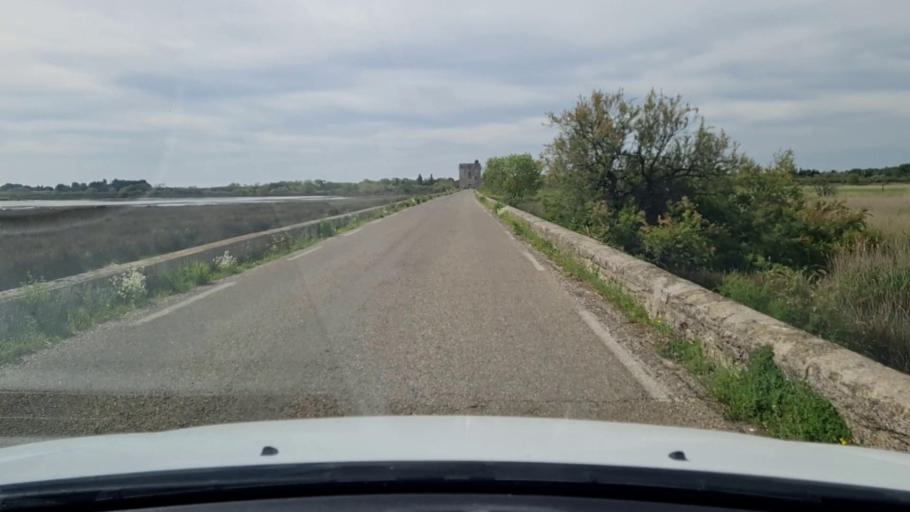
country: FR
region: Languedoc-Roussillon
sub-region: Departement du Gard
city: Aigues-Mortes
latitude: 43.5958
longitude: 4.2081
